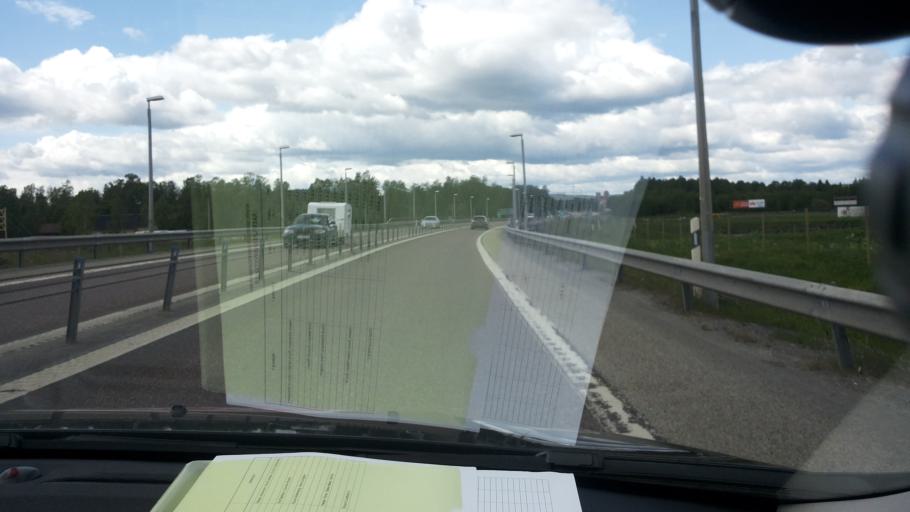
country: SE
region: Vaesternorrland
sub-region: Timra Kommun
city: Soraker
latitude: 62.5167
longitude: 17.4535
